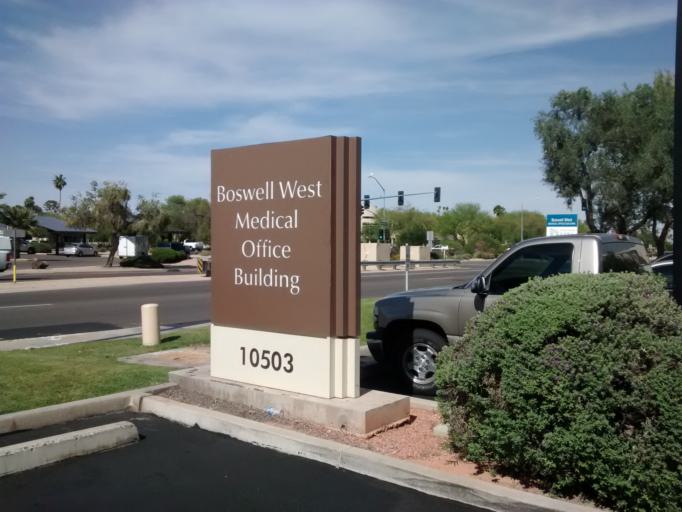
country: US
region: Arizona
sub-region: Maricopa County
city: Sun City
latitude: 33.6048
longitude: -112.2859
